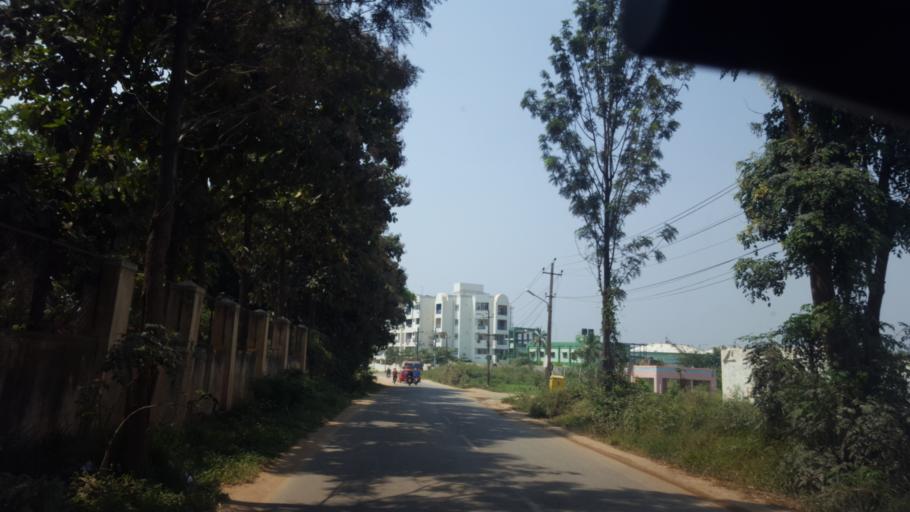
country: IN
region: Karnataka
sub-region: Bangalore Urban
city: Bangalore
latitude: 12.9390
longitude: 77.7186
